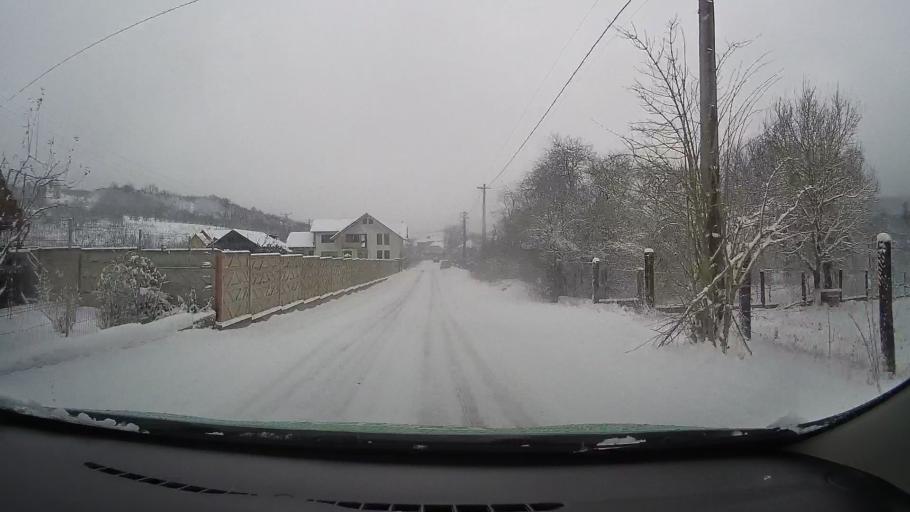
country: RO
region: Hunedoara
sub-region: Comuna Carjiti
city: Carjiti
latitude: 45.8295
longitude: 22.8459
